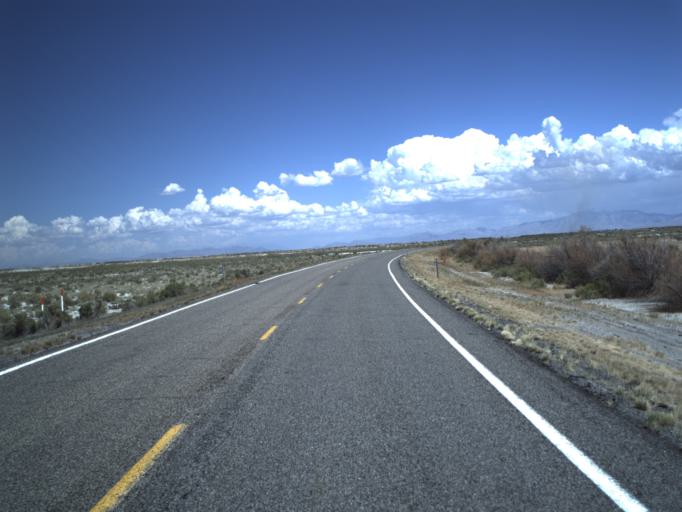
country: US
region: Utah
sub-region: Millard County
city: Delta
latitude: 39.3043
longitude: -112.8039
